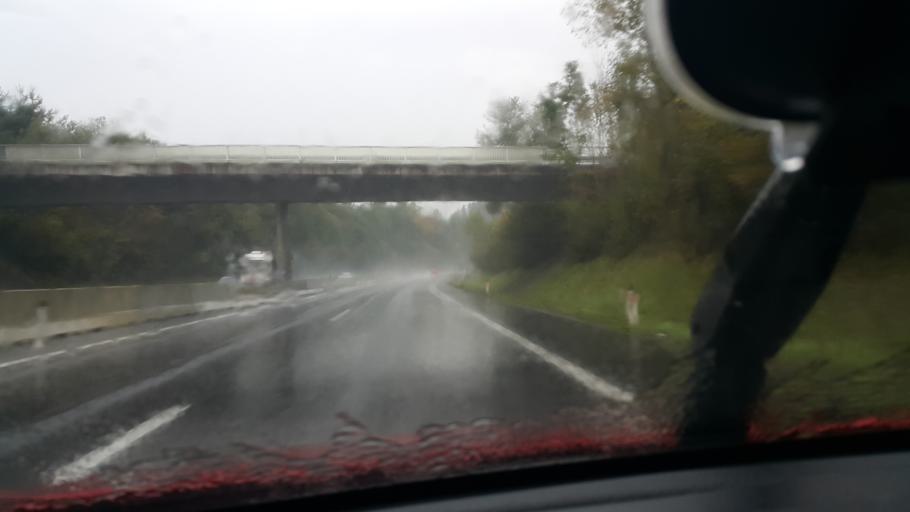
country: AT
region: Carinthia
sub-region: Politischer Bezirk Volkermarkt
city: Voelkermarkt
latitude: 46.6743
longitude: 14.5891
